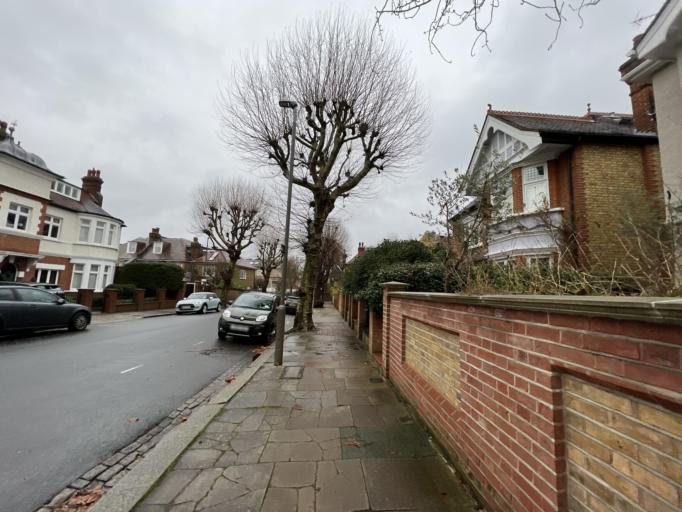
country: GB
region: England
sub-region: Greater London
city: Wandsworth
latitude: 51.4602
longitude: -0.2301
